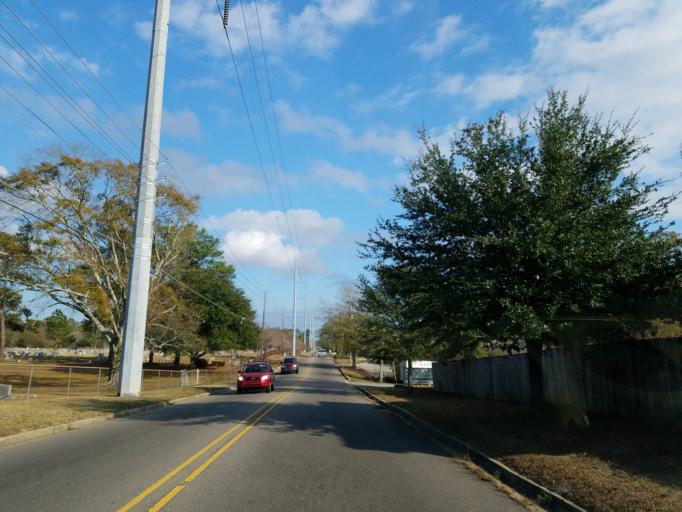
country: US
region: Mississippi
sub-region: Lamar County
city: Arnold Line
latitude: 31.3359
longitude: -89.3409
